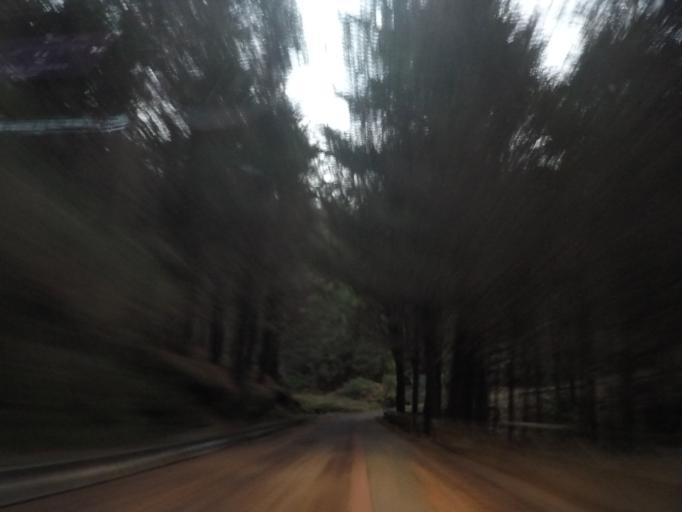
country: PT
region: Madeira
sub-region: Santa Cruz
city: Camacha
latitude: 32.7164
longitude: -16.8545
